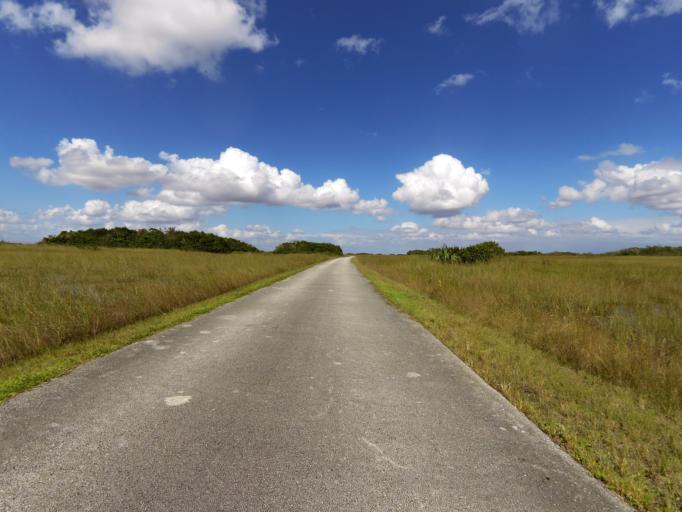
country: US
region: Florida
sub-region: Miami-Dade County
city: The Hammocks
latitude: 25.6629
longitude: -80.7623
